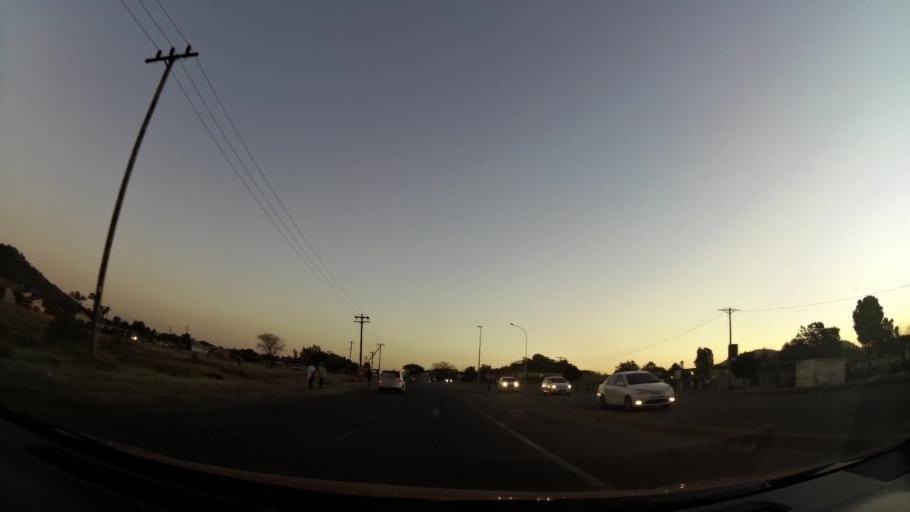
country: ZA
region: North-West
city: Ga-Rankuwa
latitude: -25.6006
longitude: 27.9736
